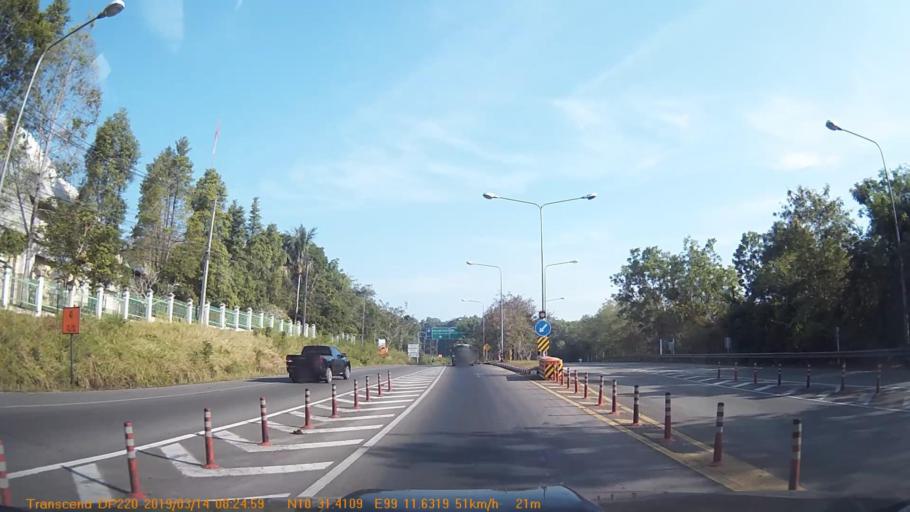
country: TH
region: Chumphon
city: Chumphon
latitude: 10.5236
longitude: 99.1939
